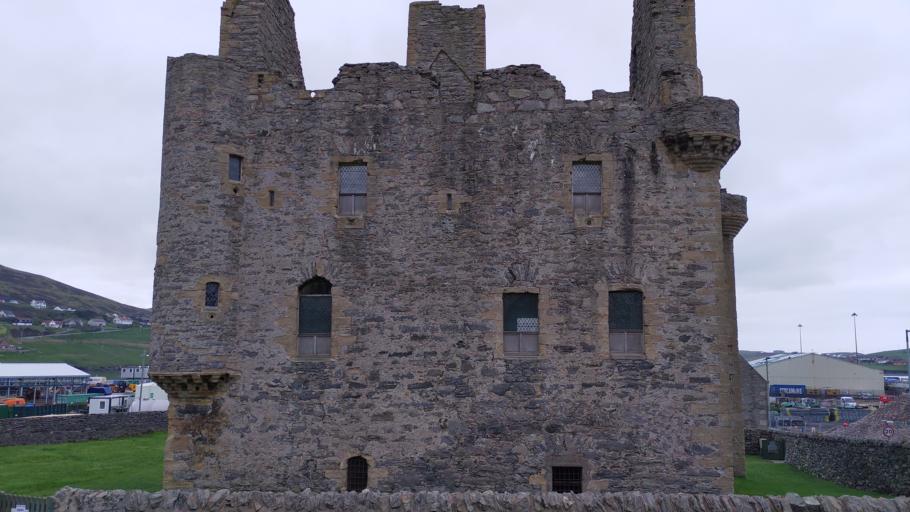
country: GB
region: Scotland
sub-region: Shetland Islands
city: Lerwick
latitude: 60.1359
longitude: -1.2741
